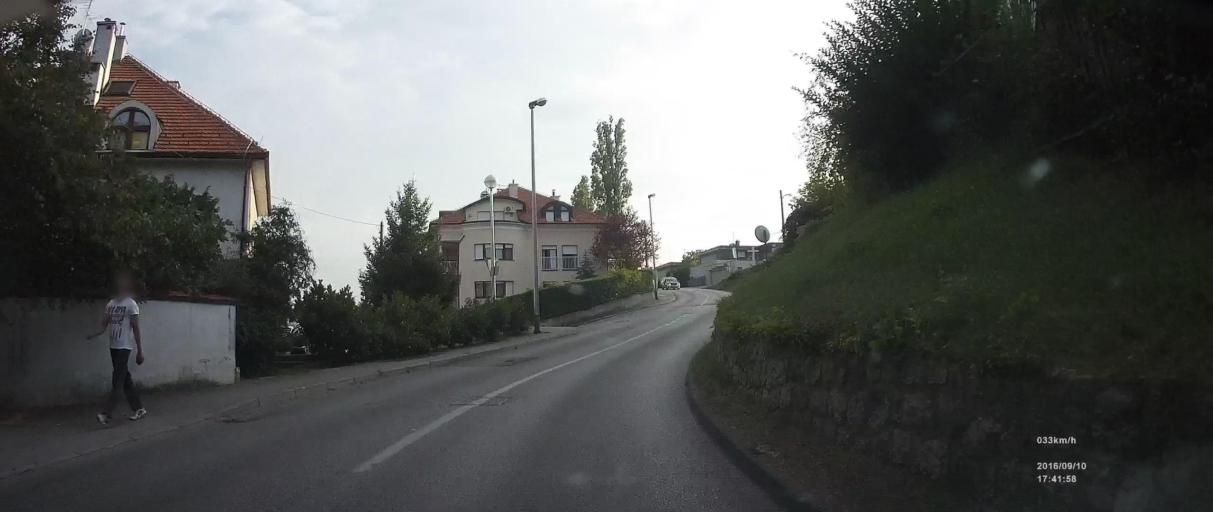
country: HR
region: Grad Zagreb
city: Zagreb
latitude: 45.8316
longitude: 15.9395
